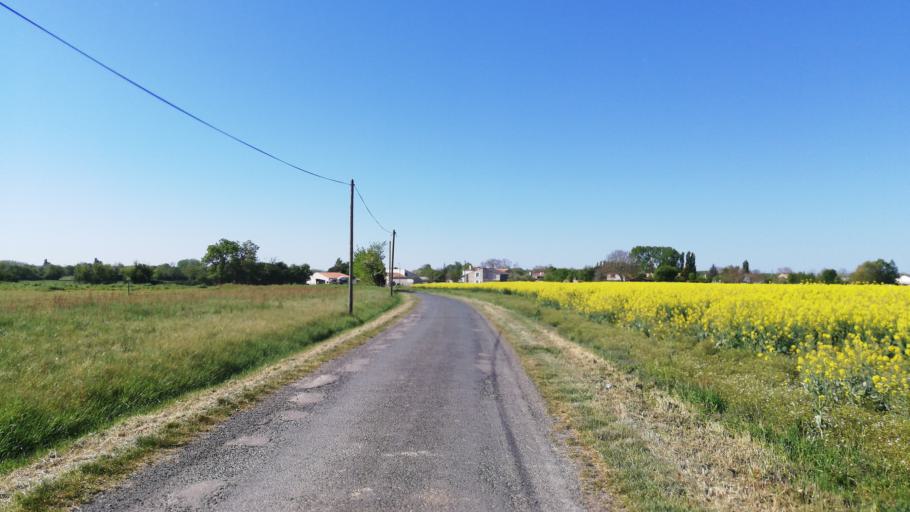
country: FR
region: Pays de la Loire
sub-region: Departement de la Vendee
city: Maillezais
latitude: 46.3260
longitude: -0.7470
